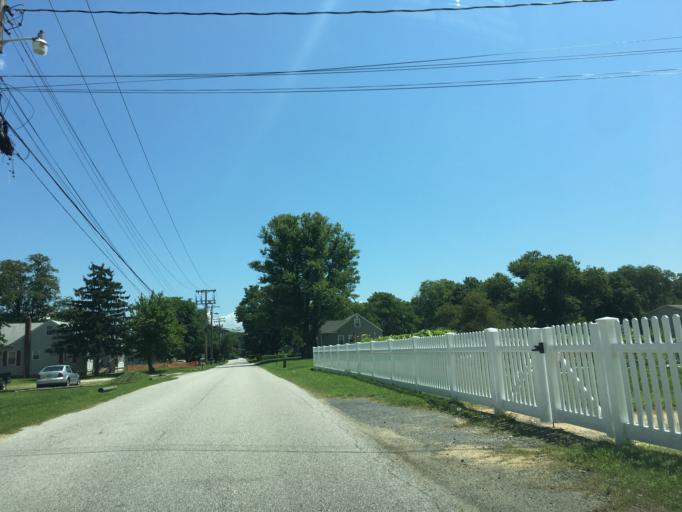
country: US
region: Maryland
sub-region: Anne Arundel County
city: Severna Park
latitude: 39.0869
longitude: -76.5577
